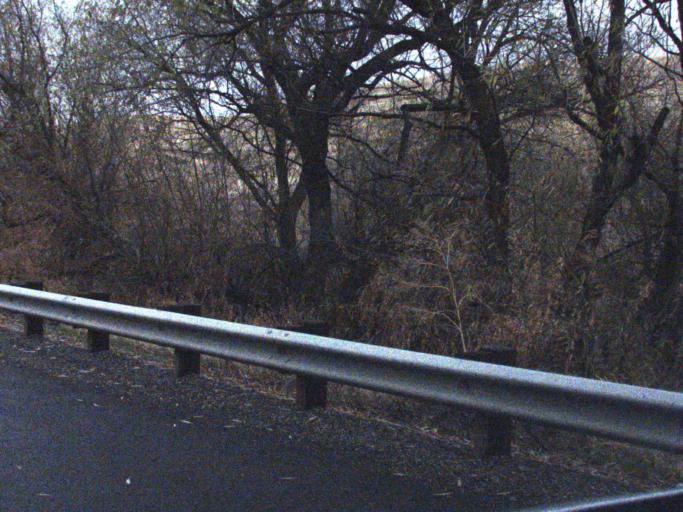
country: US
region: Washington
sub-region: Columbia County
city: Dayton
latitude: 46.4306
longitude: -117.9475
